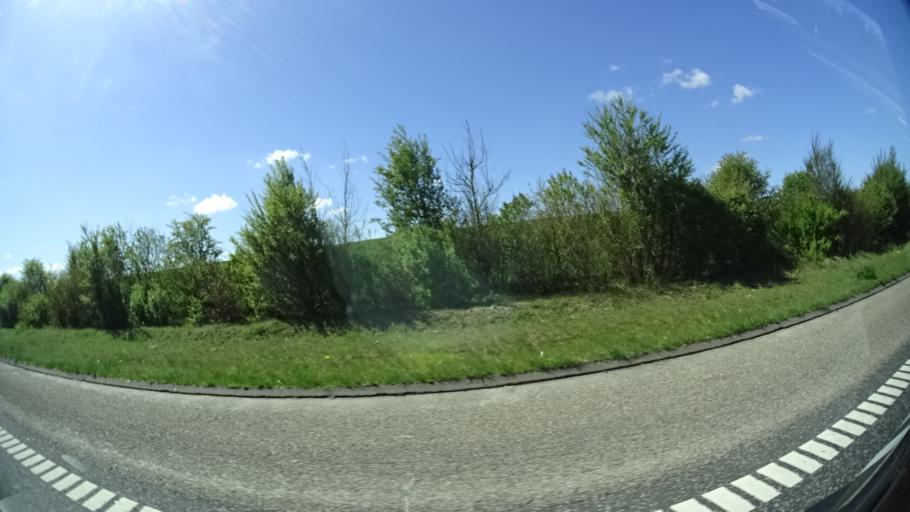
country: DK
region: Central Jutland
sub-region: Randers Kommune
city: Assentoft
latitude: 56.3704
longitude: 10.1177
